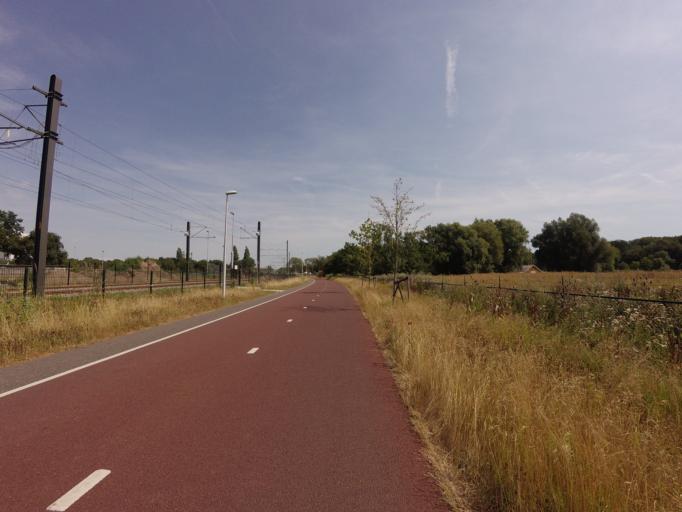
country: NL
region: Utrecht
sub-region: Gemeente Utrecht
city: Lunetten
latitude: 52.0703
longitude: 5.1463
